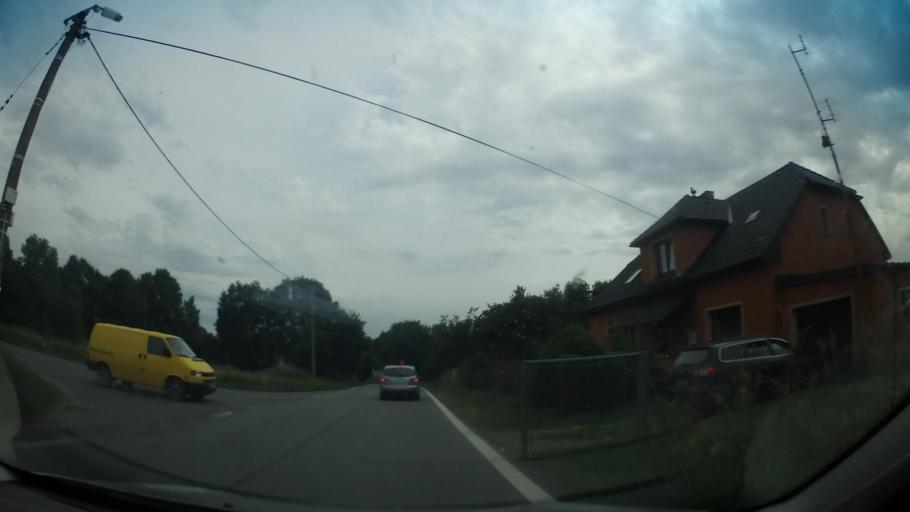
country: CZ
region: Vysocina
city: Bystrice nad Pernstejnem
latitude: 49.4963
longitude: 16.1754
